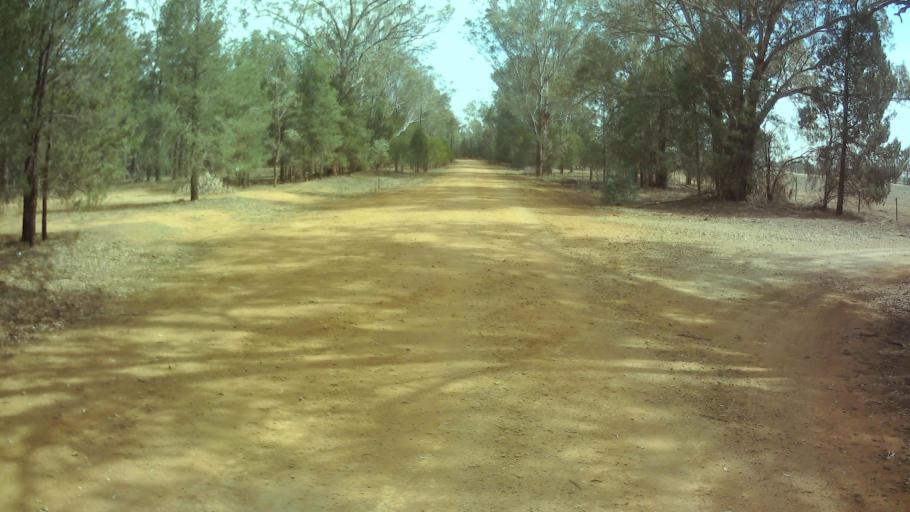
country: AU
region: New South Wales
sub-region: Weddin
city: Grenfell
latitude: -33.7112
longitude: 148.0227
